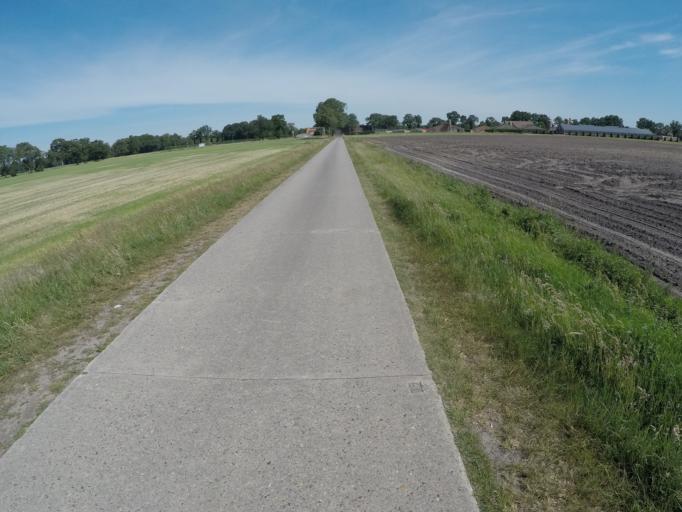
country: BE
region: Flanders
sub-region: Provincie Antwerpen
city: Kalmthout
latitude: 51.3919
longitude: 4.5241
